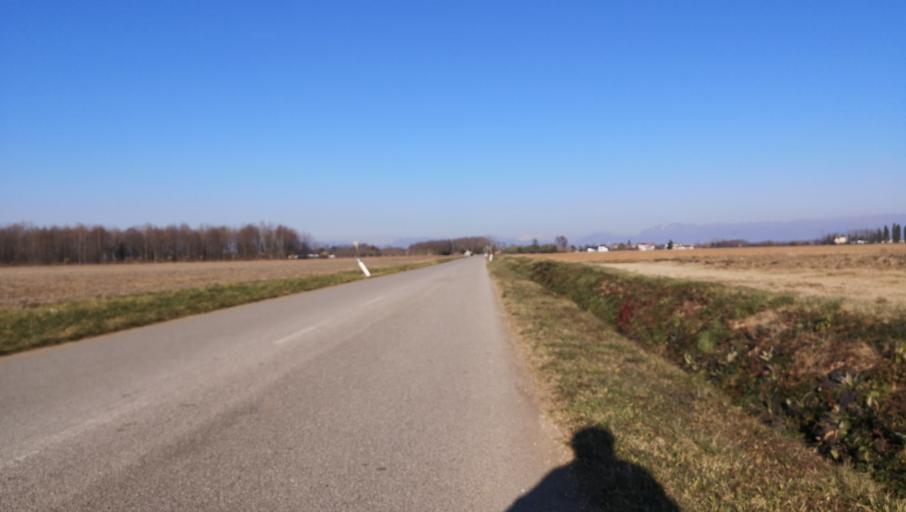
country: IT
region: Friuli Venezia Giulia
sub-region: Provincia di Udine
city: Santa Maria la Longa
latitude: 45.9457
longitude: 13.2749
